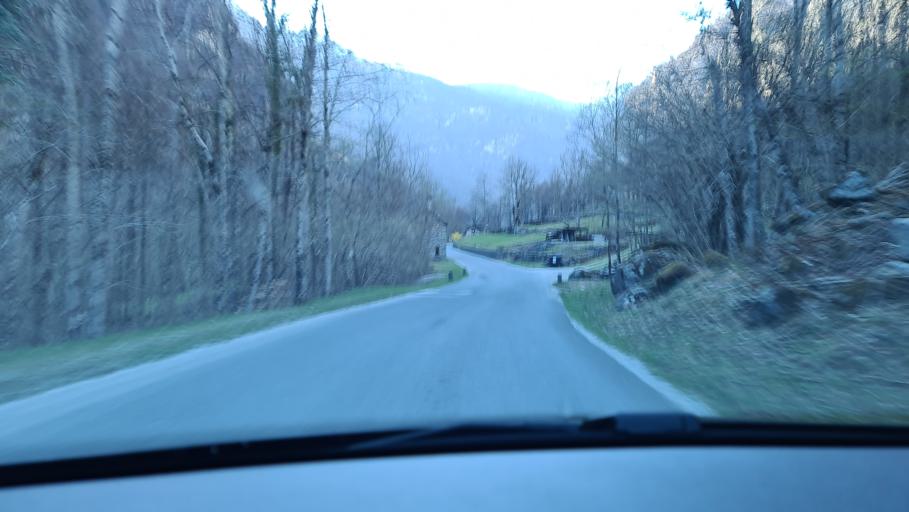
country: CH
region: Ticino
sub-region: Vallemaggia District
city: Cevio
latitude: 46.3638
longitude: 8.5702
